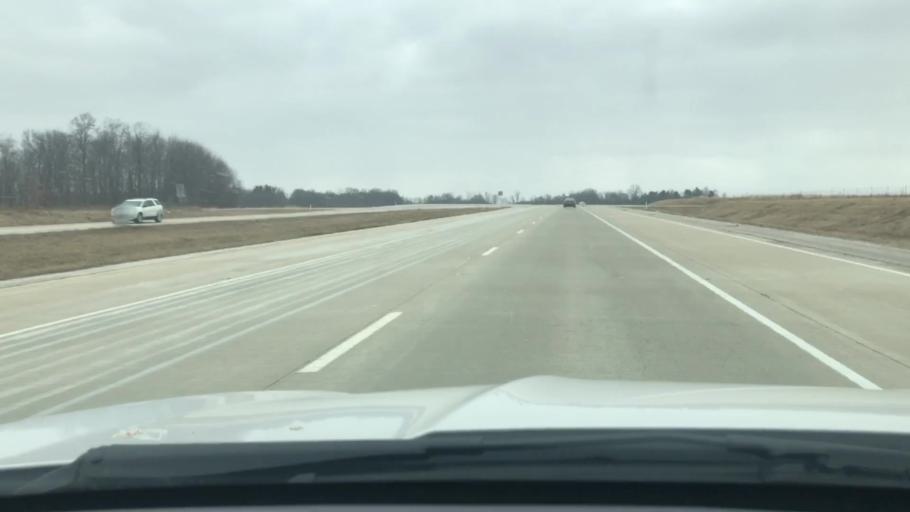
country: US
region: Indiana
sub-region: Carroll County
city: Delphi
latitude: 40.5172
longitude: -86.7209
